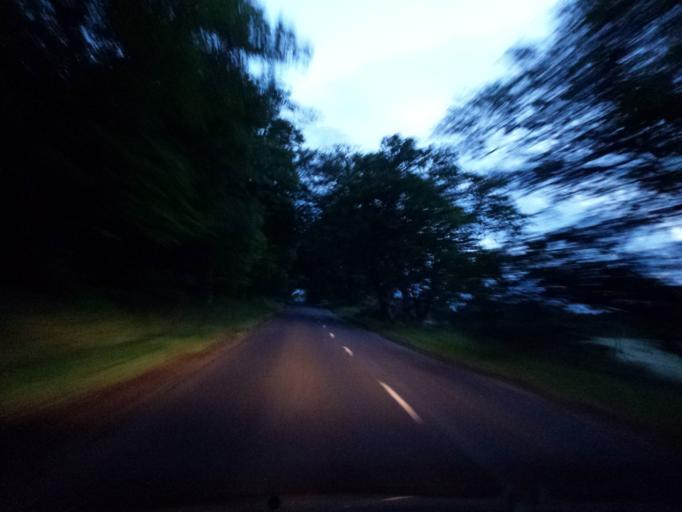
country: GB
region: Scotland
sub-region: The Scottish Borders
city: Duns
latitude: 55.7417
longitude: -2.4199
